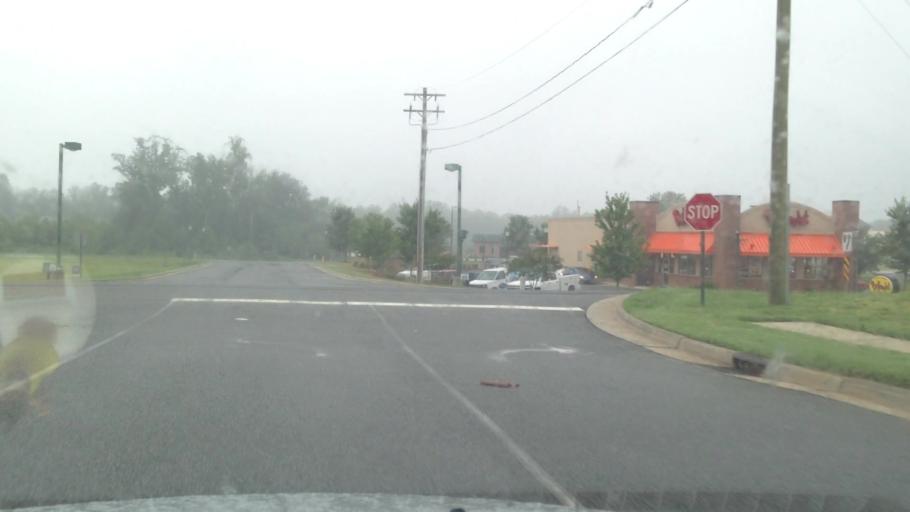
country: US
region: North Carolina
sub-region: Forsyth County
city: Walkertown
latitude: 36.1641
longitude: -80.1341
